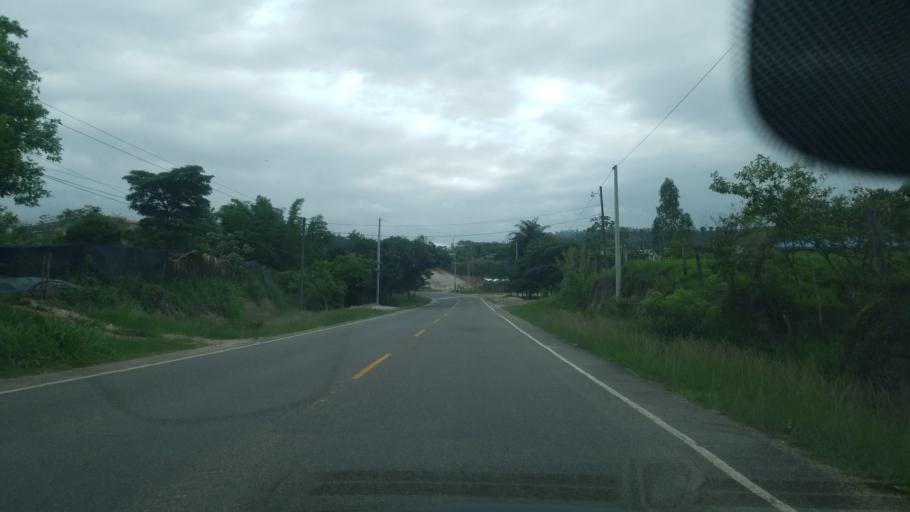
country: HN
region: Ocotepeque
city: Lucerna
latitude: 14.5602
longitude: -88.9370
